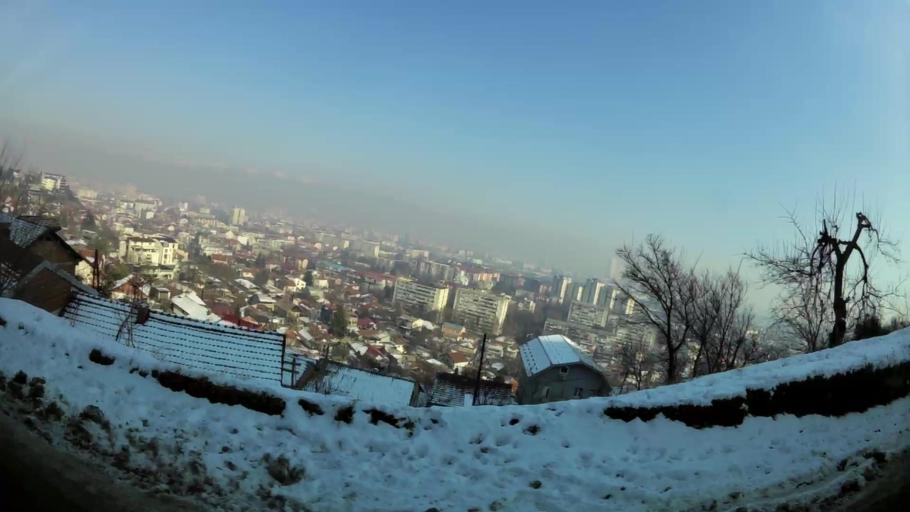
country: MK
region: Sopiste
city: Sopishte
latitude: 41.9712
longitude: 21.4372
